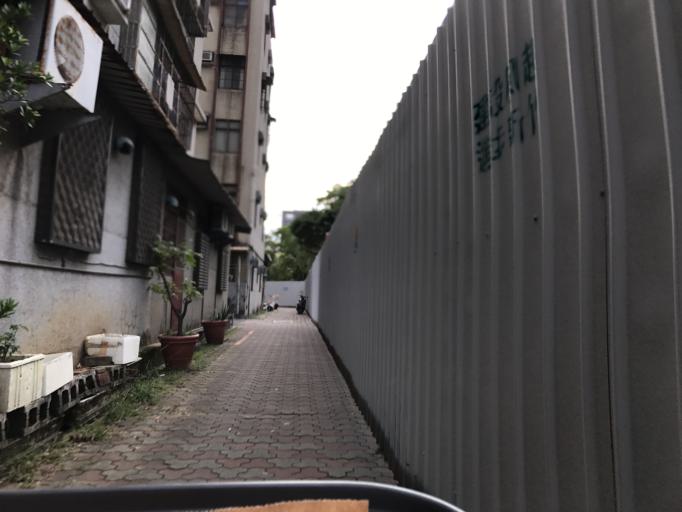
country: TW
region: Taiwan
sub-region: Hsinchu
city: Hsinchu
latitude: 24.8135
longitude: 120.9693
